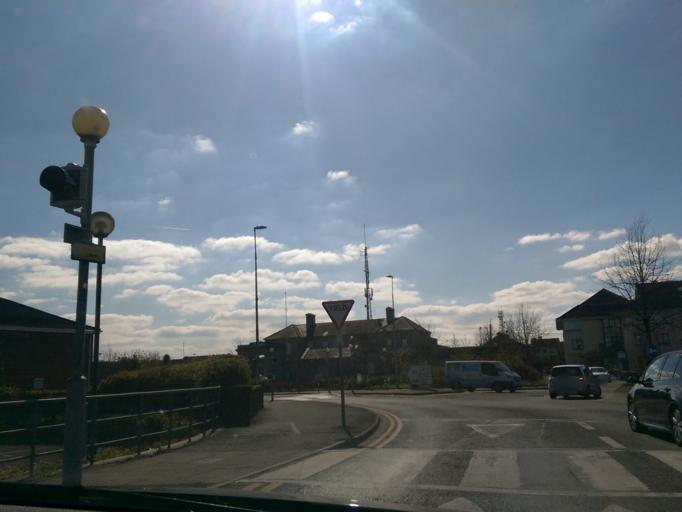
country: IE
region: Leinster
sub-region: Laois
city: Portlaoise
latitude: 53.0323
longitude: -7.3016
